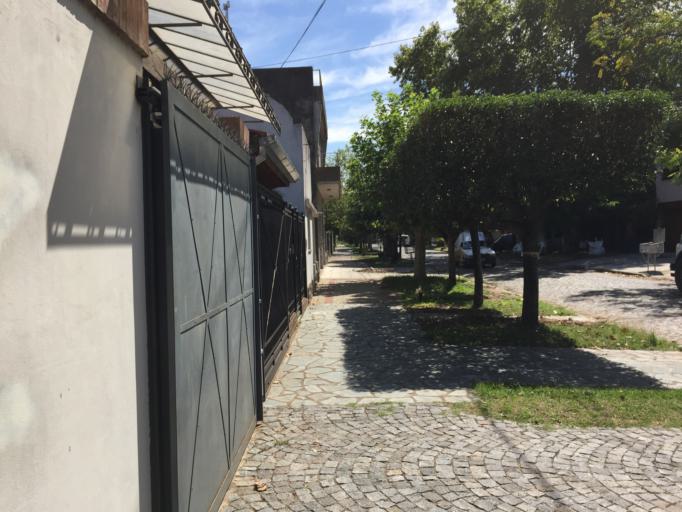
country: AR
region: Buenos Aires
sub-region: Partido de Lomas de Zamora
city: Lomas de Zamora
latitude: -34.7425
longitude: -58.3842
